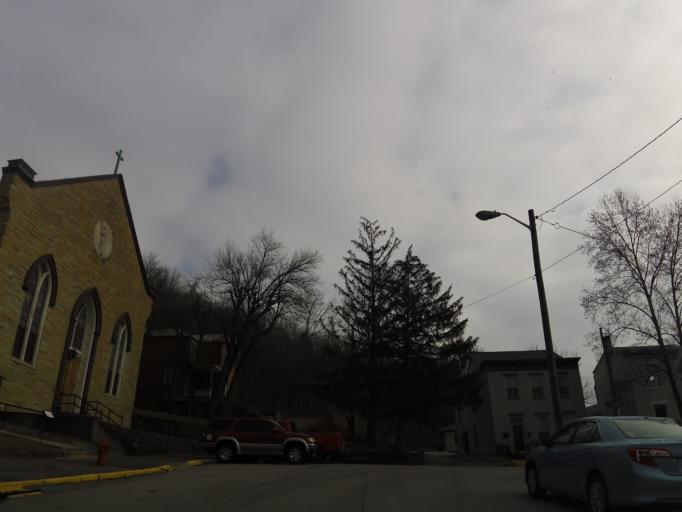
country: US
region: Indiana
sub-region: Jefferson County
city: Madison
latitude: 38.7375
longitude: -85.3734
